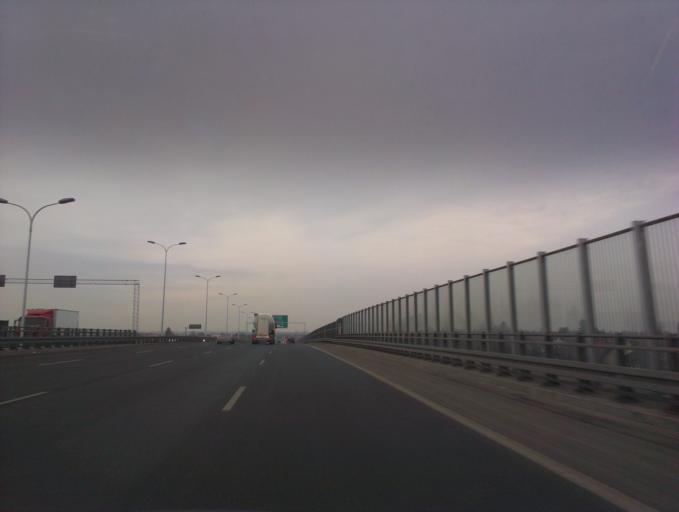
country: PL
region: Masovian Voivodeship
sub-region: Powiat pruszkowski
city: Nowe Grocholice
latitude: 52.1847
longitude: 20.9163
